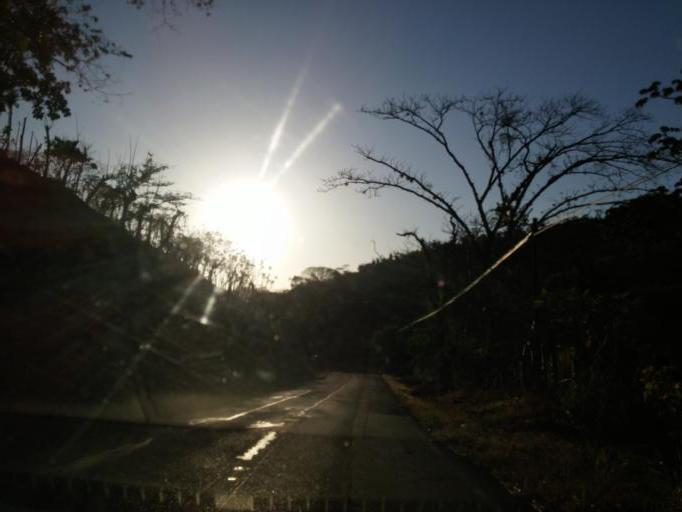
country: CR
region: Alajuela
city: Desamparados
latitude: 9.9523
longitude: -84.4953
